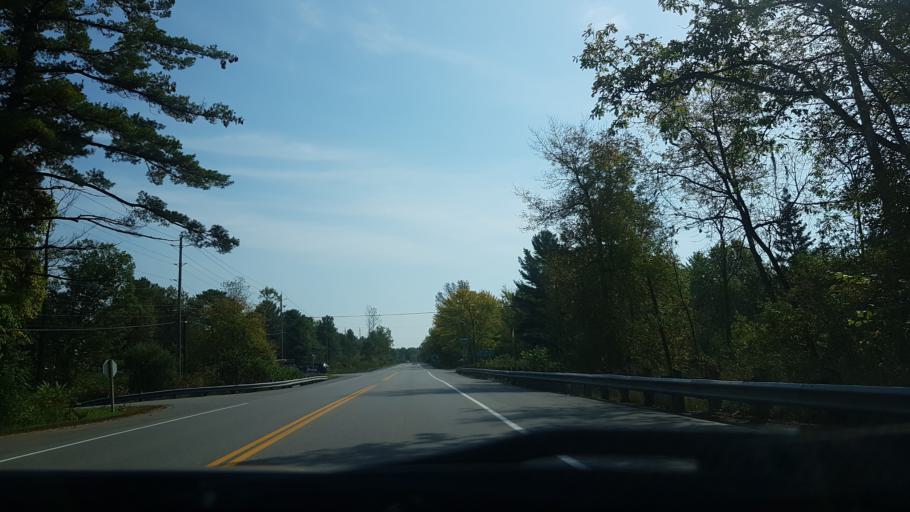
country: CA
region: Ontario
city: Orillia
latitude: 44.7462
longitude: -79.3238
